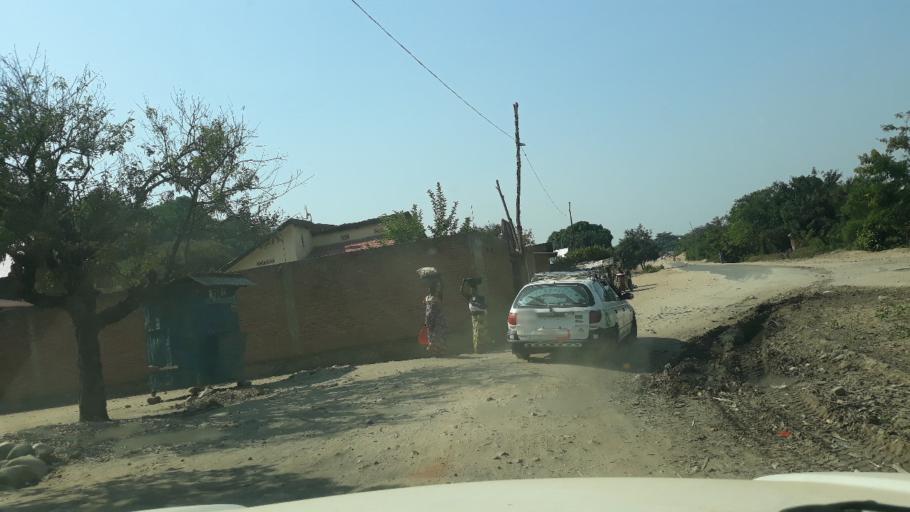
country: CD
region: South Kivu
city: Uvira
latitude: -3.2393
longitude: 29.1618
